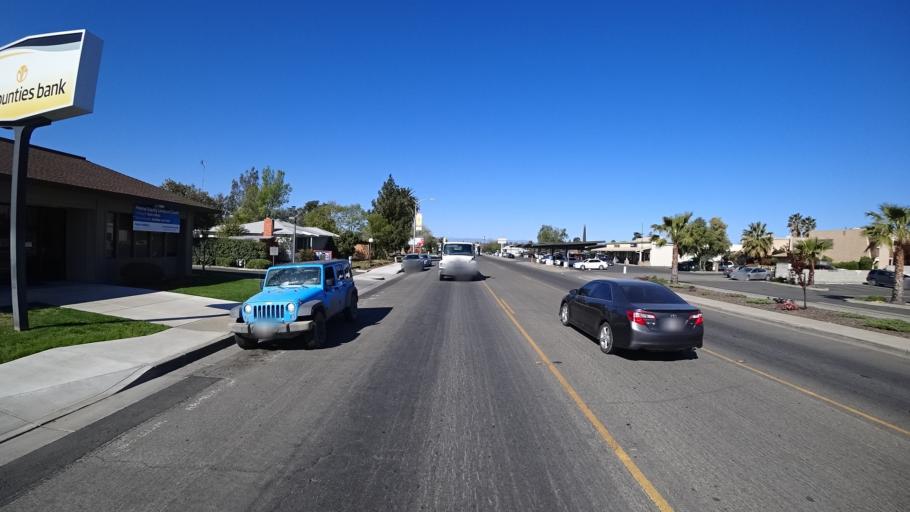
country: US
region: California
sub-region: Glenn County
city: Orland
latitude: 39.7473
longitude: -122.1844
